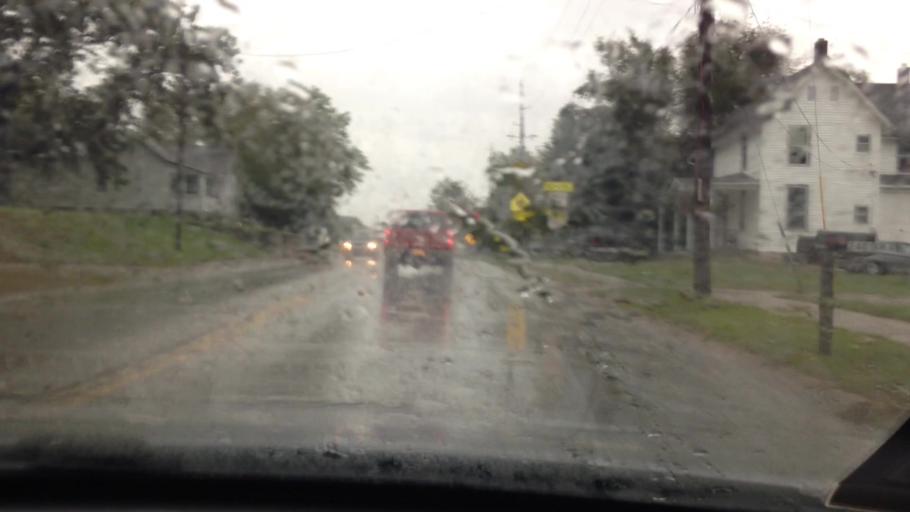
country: US
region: Kansas
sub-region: Leavenworth County
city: Leavenworth
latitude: 39.2929
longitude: -94.9137
